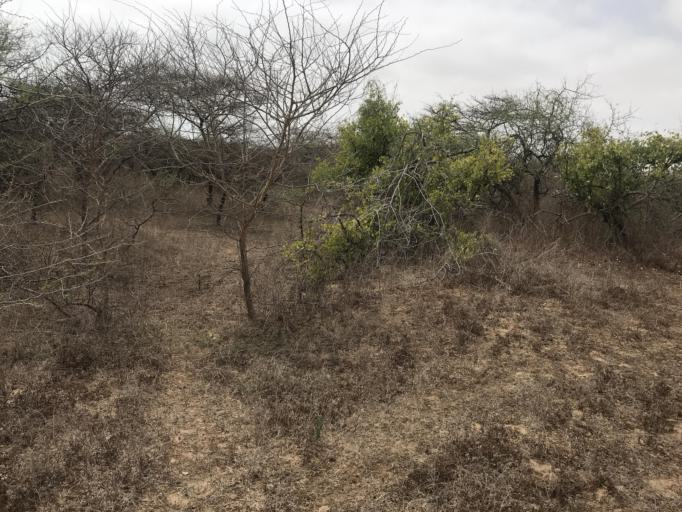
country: SN
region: Saint-Louis
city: Saint-Louis
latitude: 15.9096
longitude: -16.4567
